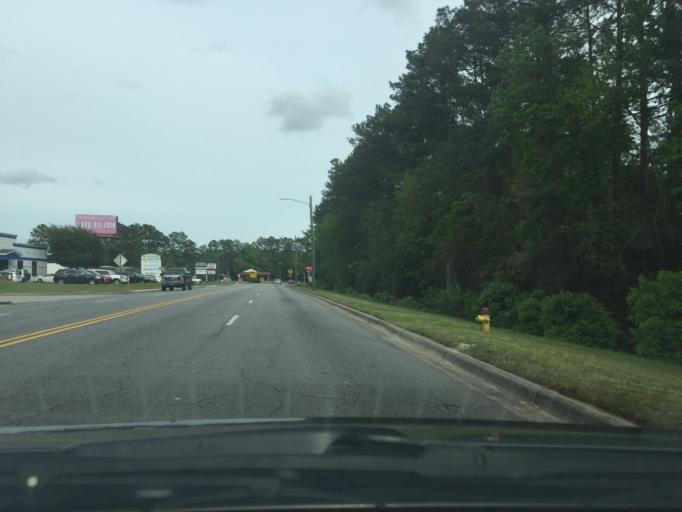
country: US
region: Georgia
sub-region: Chatham County
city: Isle of Hope
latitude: 32.0011
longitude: -81.1084
